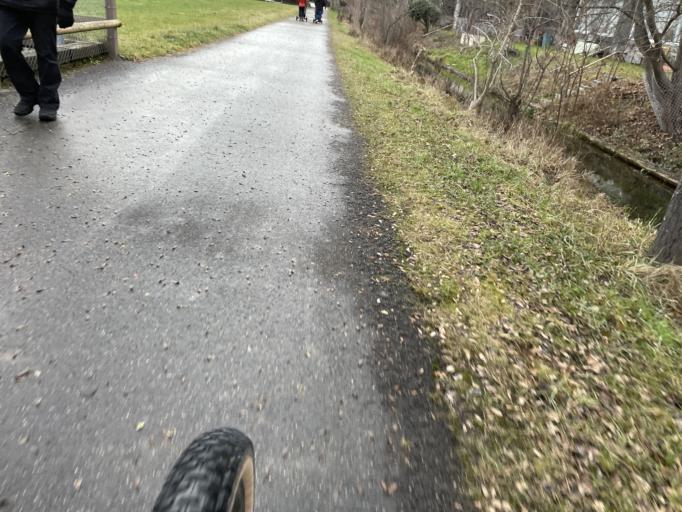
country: CH
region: Bern
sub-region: Bern-Mittelland District
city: Munsingen
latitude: 46.8748
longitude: 7.5470
